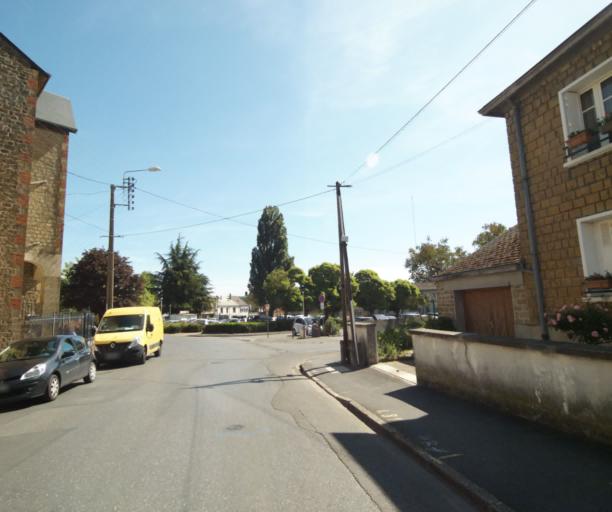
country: FR
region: Champagne-Ardenne
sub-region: Departement des Ardennes
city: Charleville-Mezieres
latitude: 49.7519
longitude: 4.7269
